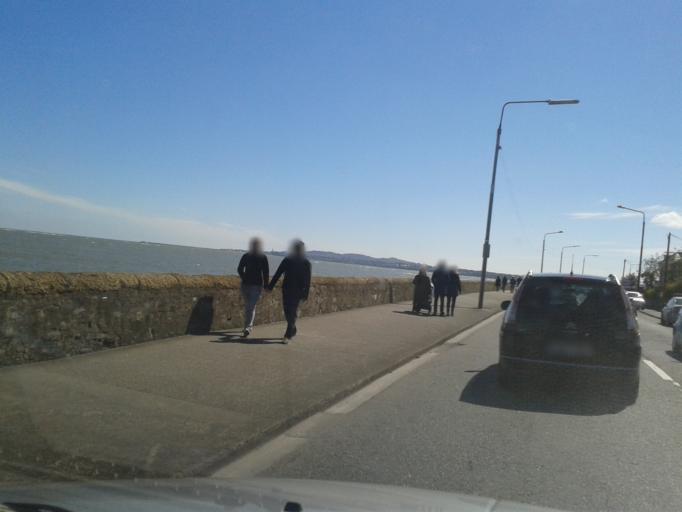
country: IE
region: Leinster
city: Sandymount
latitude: 53.3315
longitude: -6.2100
